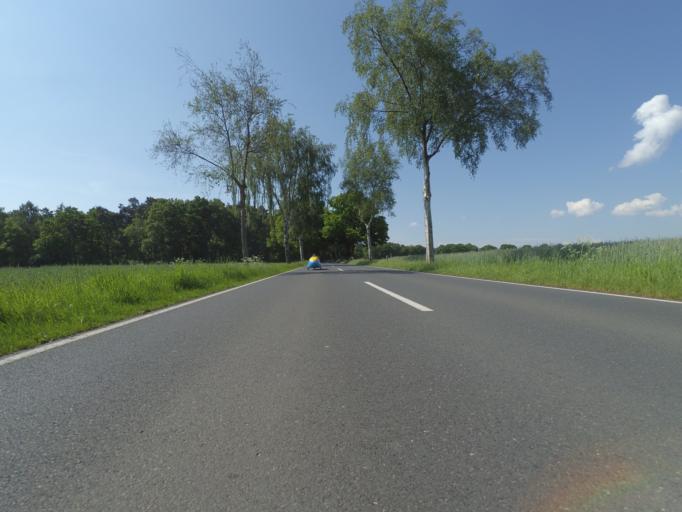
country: DE
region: Lower Saxony
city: Isernhagen Farster Bauerschaft
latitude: 52.4749
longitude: 9.8958
